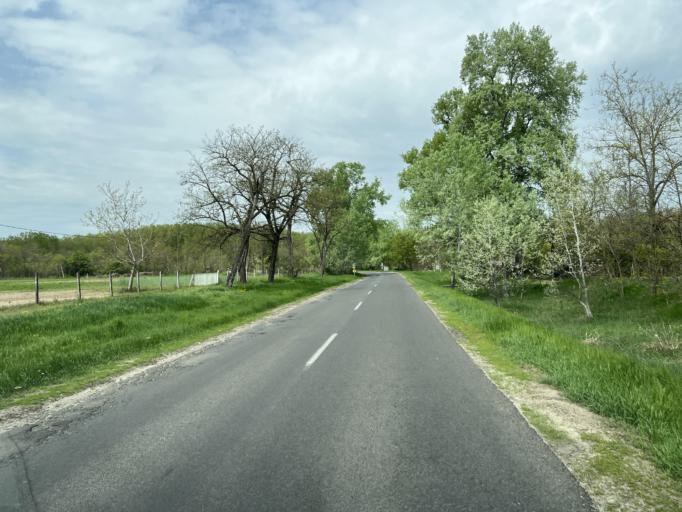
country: HU
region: Pest
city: Tortel
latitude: 47.1423
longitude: 19.8807
